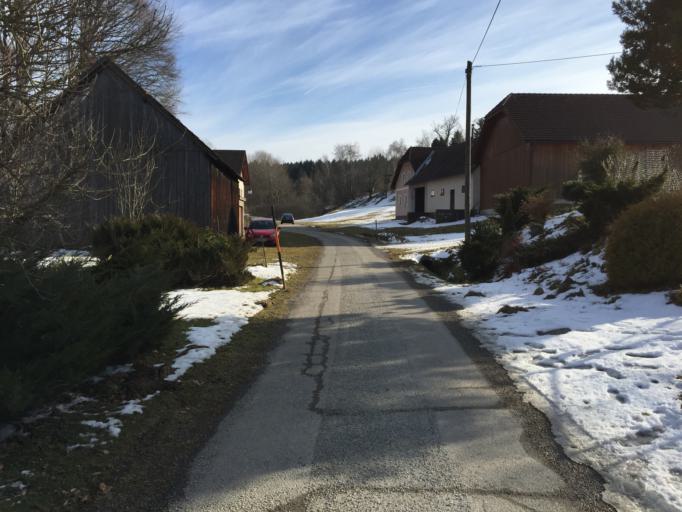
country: AT
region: Lower Austria
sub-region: Politischer Bezirk Gmund
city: Weitra
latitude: 48.6641
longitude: 14.9323
